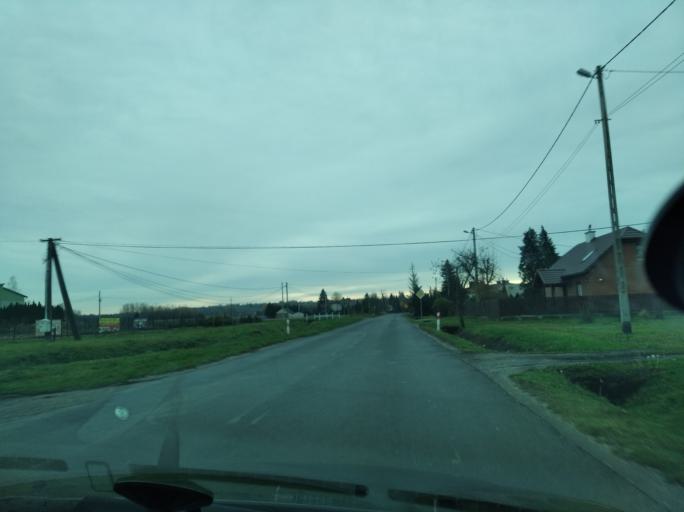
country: PL
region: Subcarpathian Voivodeship
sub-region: Powiat lancucki
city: Czarna
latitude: 50.0878
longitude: 22.1861
